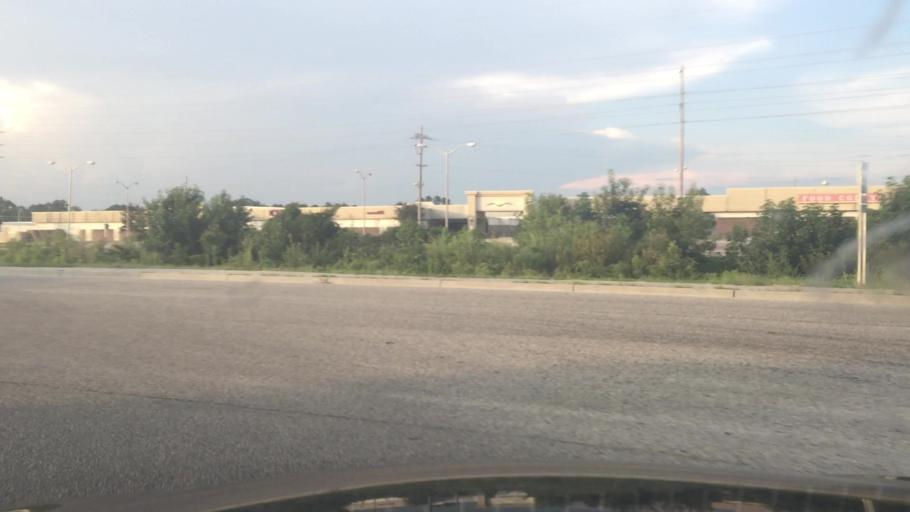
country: US
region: South Carolina
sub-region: Horry County
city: Forestbrook
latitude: 33.7136
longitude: -78.9280
